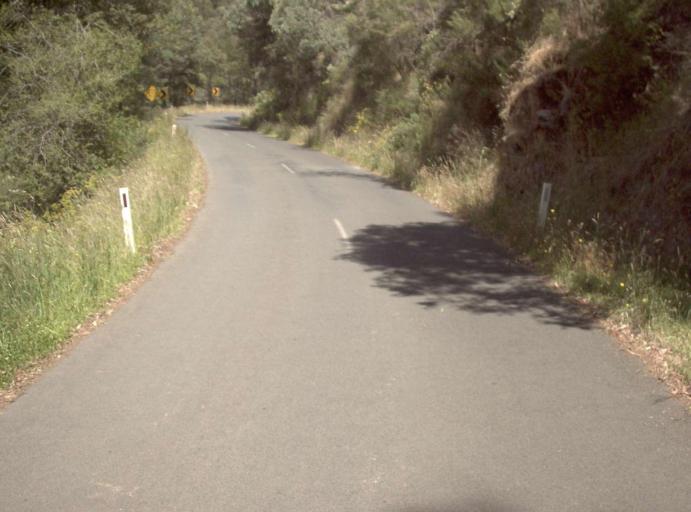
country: AU
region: Victoria
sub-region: Latrobe
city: Traralgon
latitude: -37.9510
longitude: 146.4475
